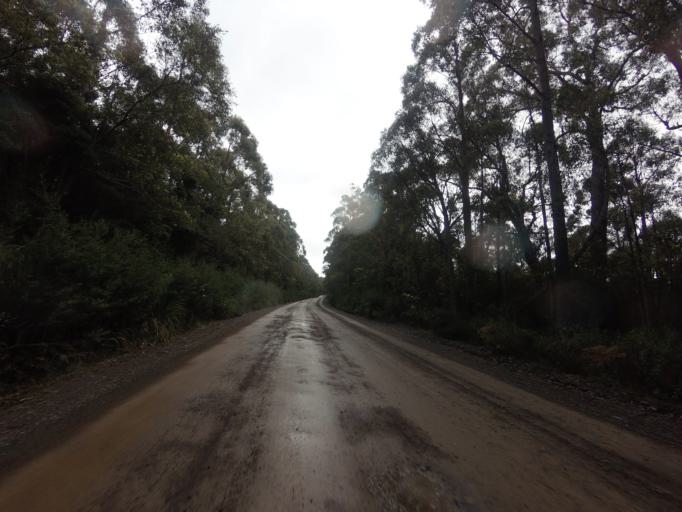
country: AU
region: Tasmania
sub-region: Huon Valley
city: Geeveston
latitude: -43.4636
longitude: 146.8998
